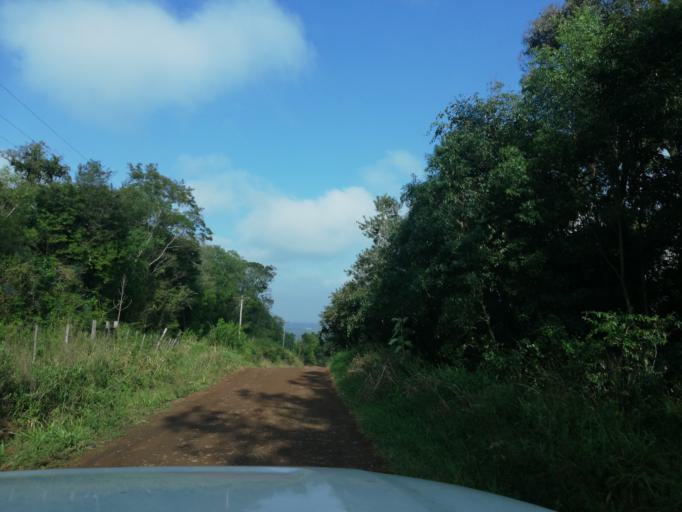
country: AR
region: Misiones
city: Cerro Azul
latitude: -27.5785
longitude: -55.5109
